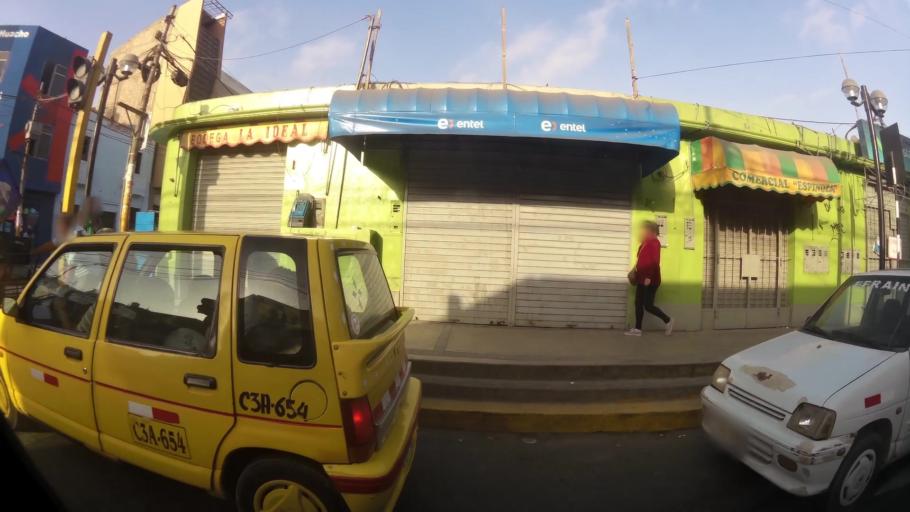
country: PE
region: Lima
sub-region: Huaura
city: Huacho
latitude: -11.1064
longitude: -77.6101
